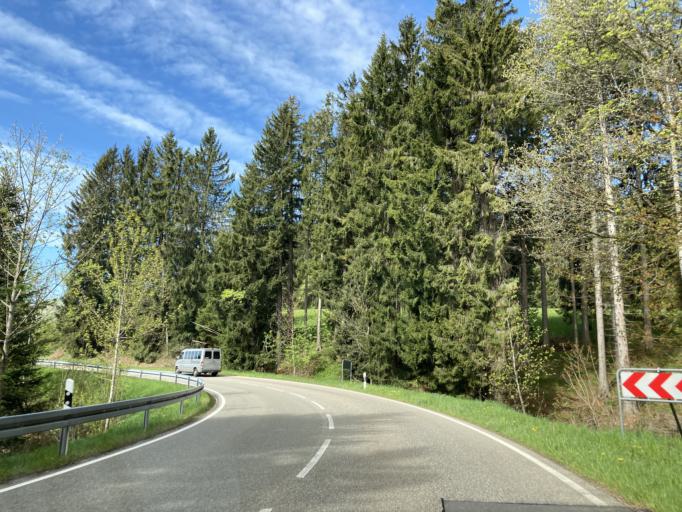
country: DE
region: Baden-Wuerttemberg
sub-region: Freiburg Region
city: Schonwald im Schwarzwald
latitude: 48.0944
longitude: 8.2049
